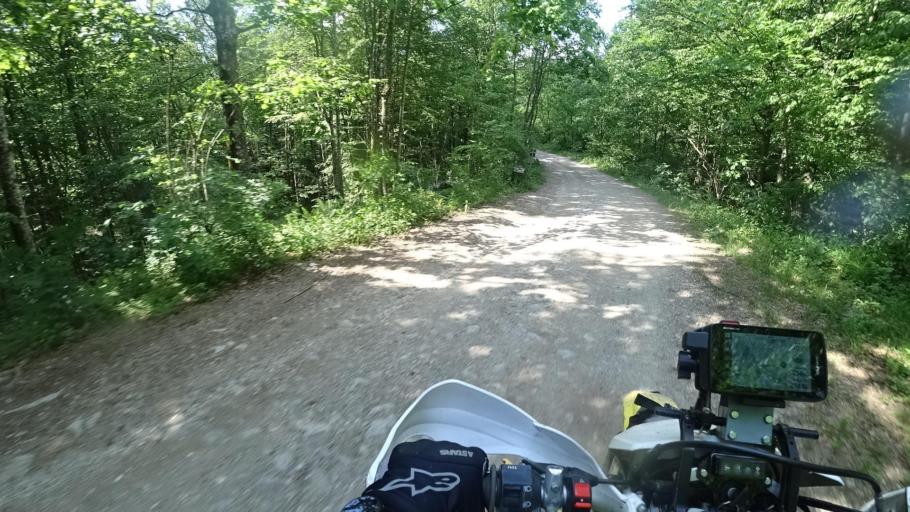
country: BA
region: Federation of Bosnia and Herzegovina
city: Bosanska Krupa
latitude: 44.7539
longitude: 16.2684
